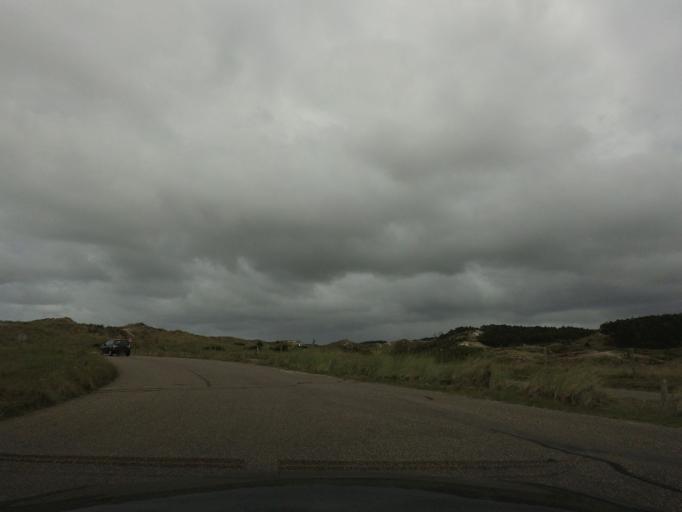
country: NL
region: North Holland
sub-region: Gemeente Bergen
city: Egmond aan Zee
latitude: 52.7139
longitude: 4.6447
